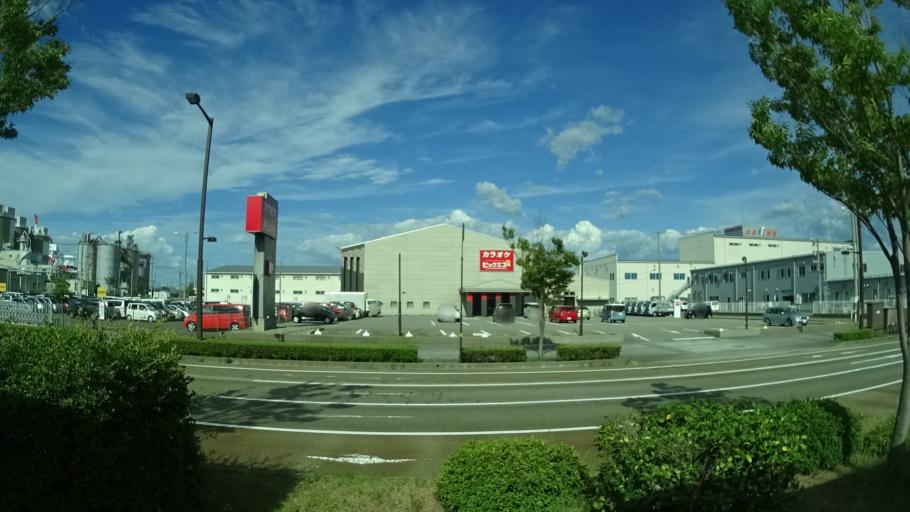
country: JP
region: Ishikawa
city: Kanazawa-shi
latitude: 36.6064
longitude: 136.6183
